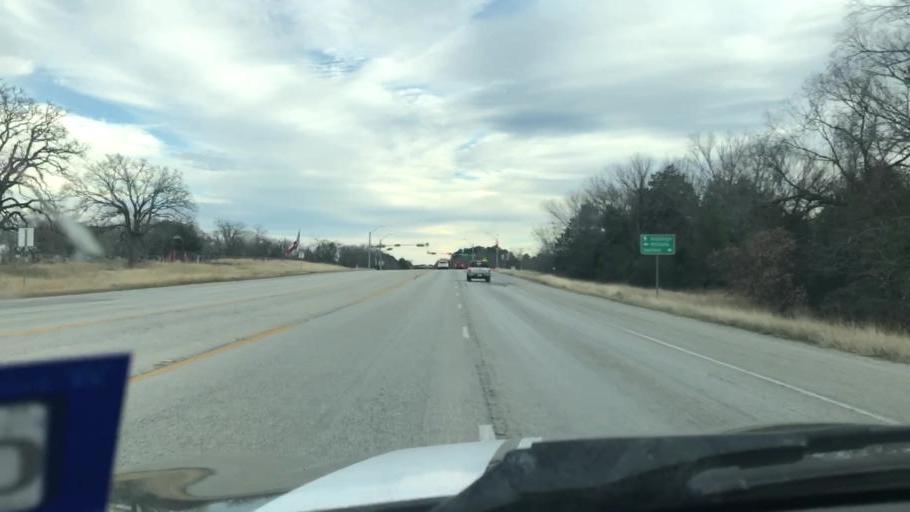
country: US
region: Texas
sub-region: Bastrop County
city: Camp Swift
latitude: 30.2811
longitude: -97.2436
